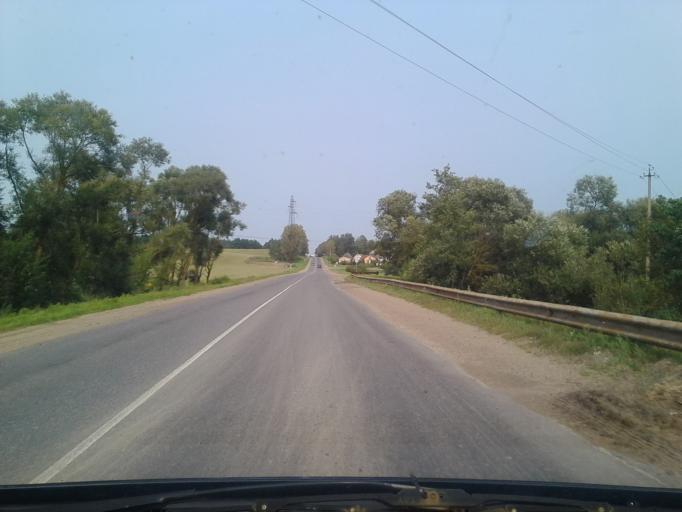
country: BY
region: Minsk
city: Hatava
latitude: 53.8019
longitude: 27.6456
